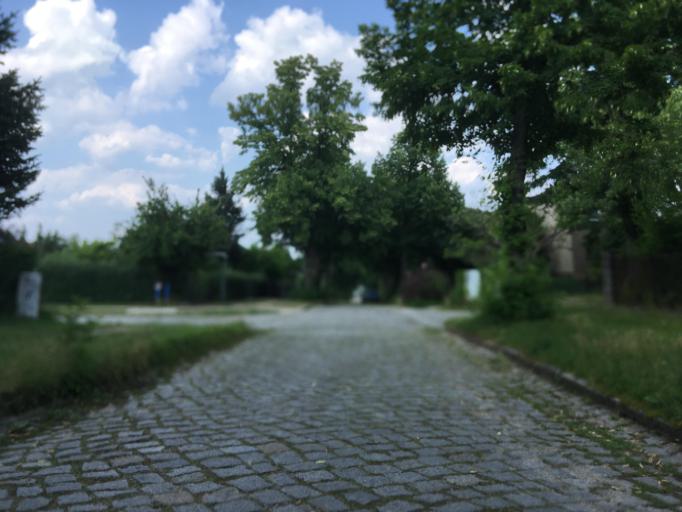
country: DE
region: Brandenburg
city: Bernau bei Berlin
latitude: 52.6504
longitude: 13.5468
